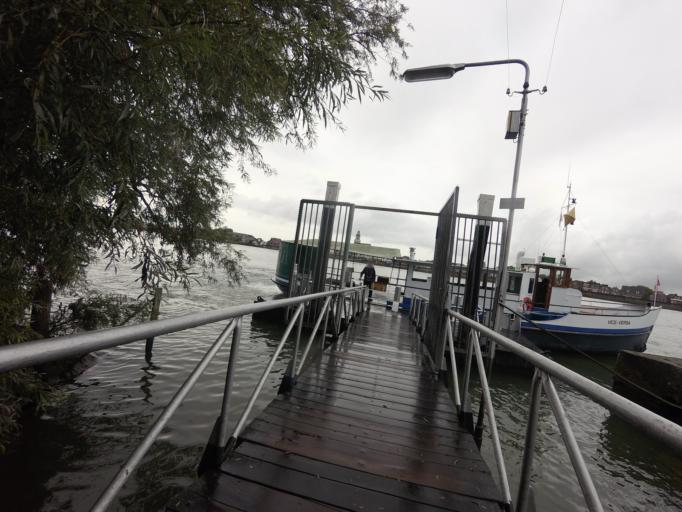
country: NL
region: South Holland
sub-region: Molenwaard
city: Nieuw-Lekkerland
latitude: 51.8928
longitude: 4.6864
